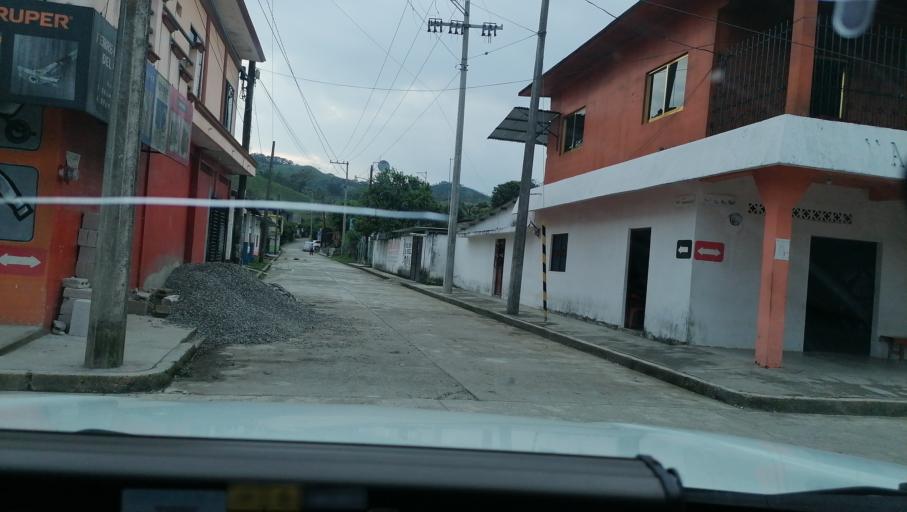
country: MX
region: Chiapas
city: Ixtacomitan
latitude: 17.3397
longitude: -93.1303
